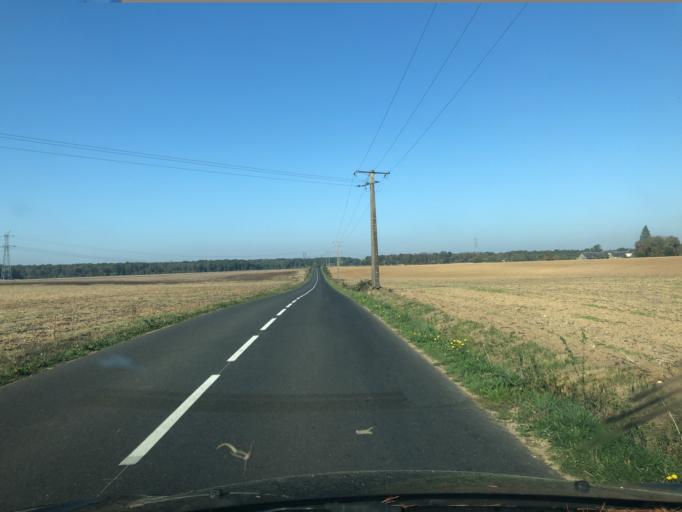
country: FR
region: Centre
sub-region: Departement d'Indre-et-Loire
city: Rouziers-de-Touraine
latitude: 47.5236
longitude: 0.6447
